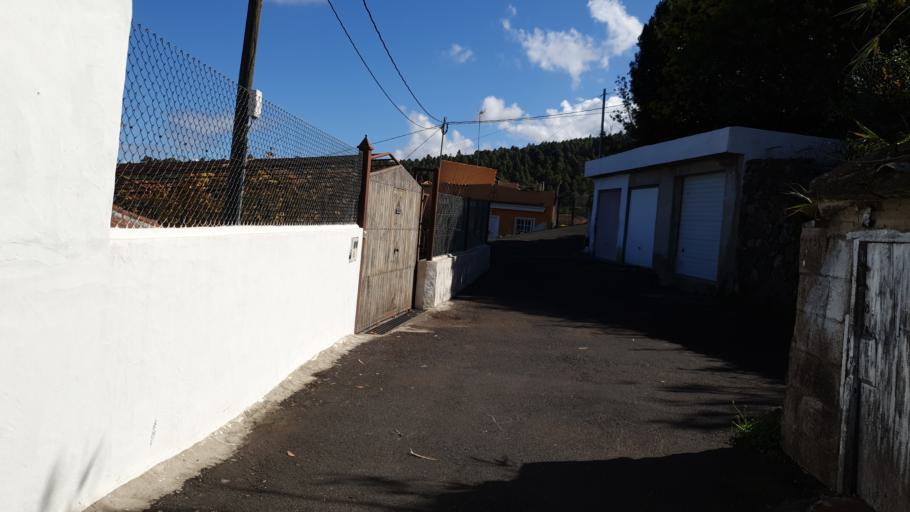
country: ES
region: Canary Islands
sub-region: Provincia de Santa Cruz de Tenerife
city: La Guancha
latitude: 28.3584
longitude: -16.6847
